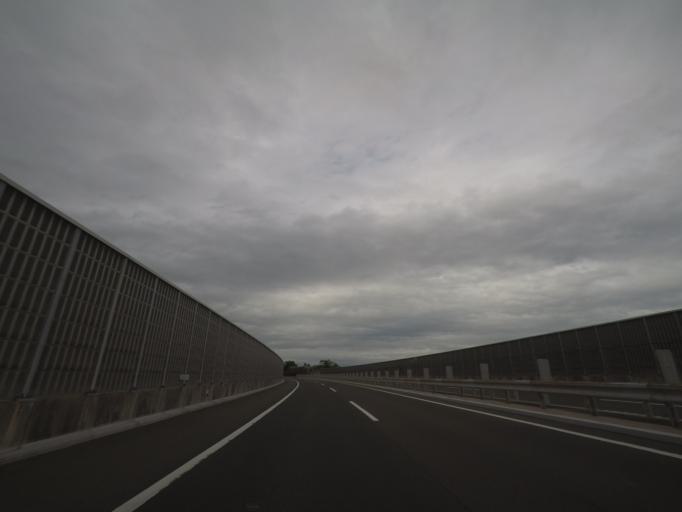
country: JP
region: Kagawa
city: Sakaidecho
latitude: 34.3135
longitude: 133.8393
